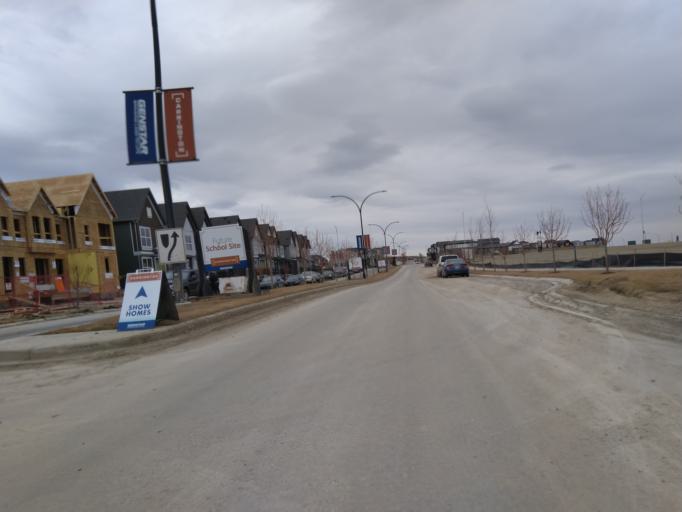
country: CA
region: Alberta
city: Airdrie
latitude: 51.1819
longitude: -114.0756
